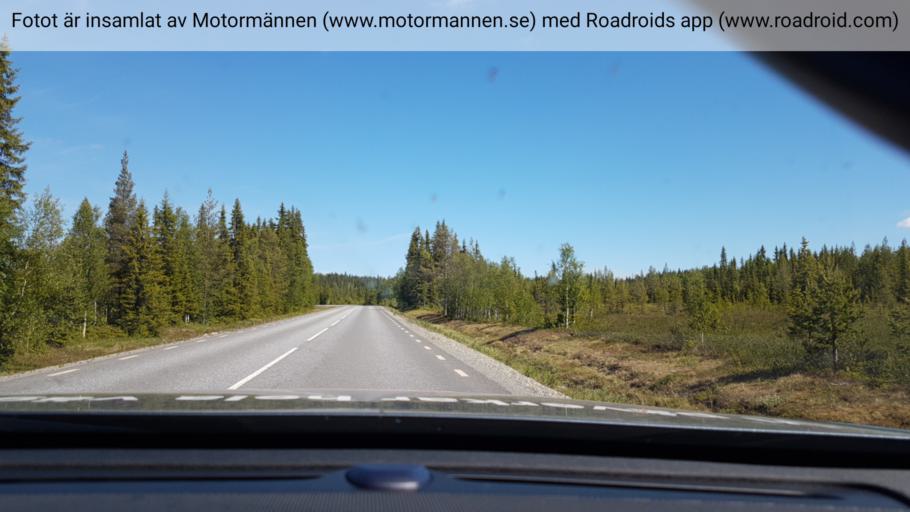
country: SE
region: Vaesterbotten
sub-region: Asele Kommun
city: Insjon
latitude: 64.7039
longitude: 17.2407
